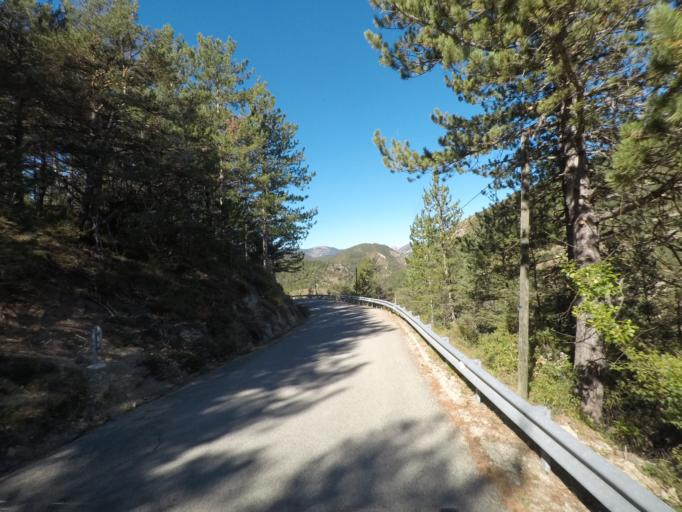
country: FR
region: Rhone-Alpes
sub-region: Departement de la Drome
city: Die
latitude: 44.5608
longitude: 5.3320
